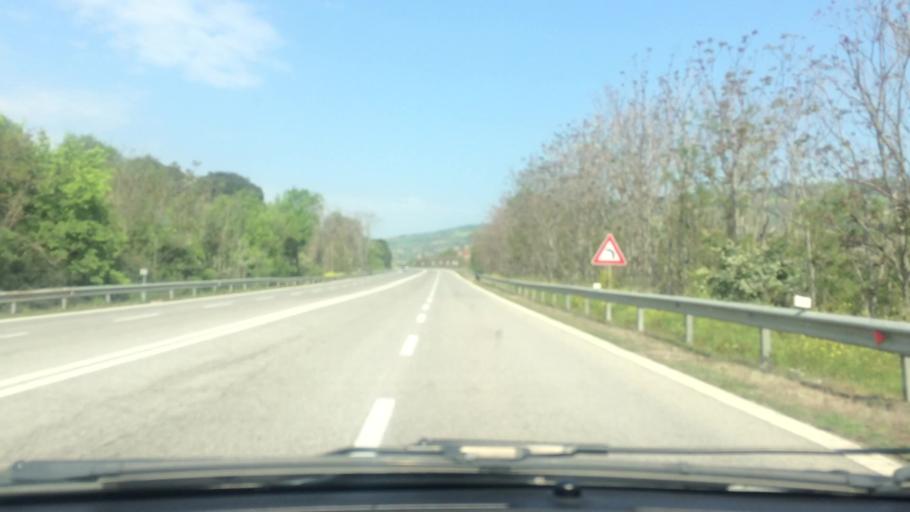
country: IT
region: Basilicate
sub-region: Provincia di Matera
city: Grottole
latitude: 40.5774
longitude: 16.3719
